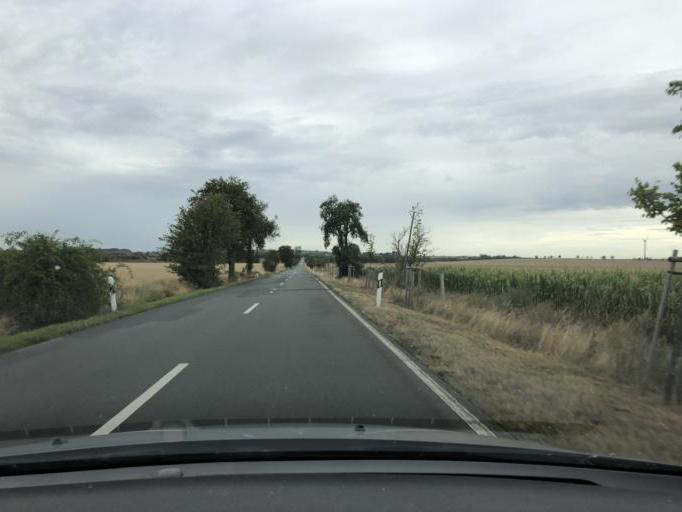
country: DE
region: Saxony-Anhalt
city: Brumby
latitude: 51.8757
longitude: 11.7126
